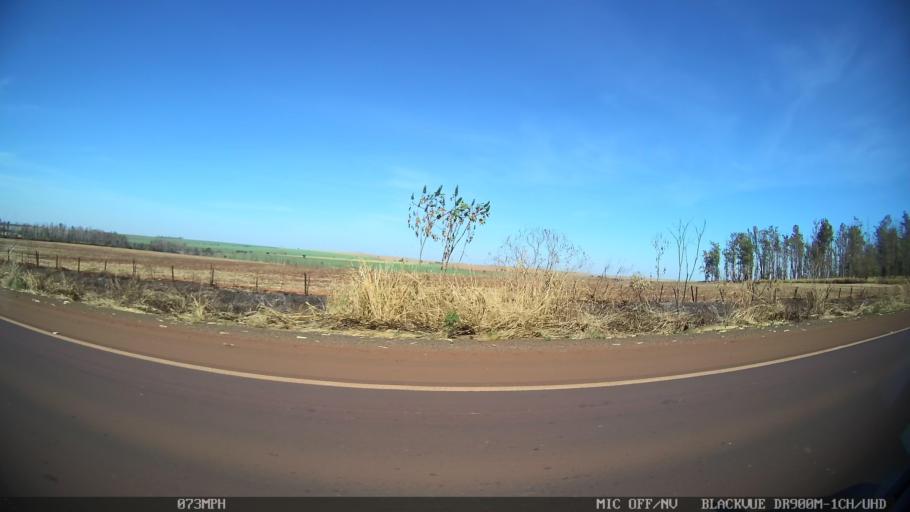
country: BR
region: Sao Paulo
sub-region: Barretos
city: Barretos
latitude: -20.4899
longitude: -48.5209
